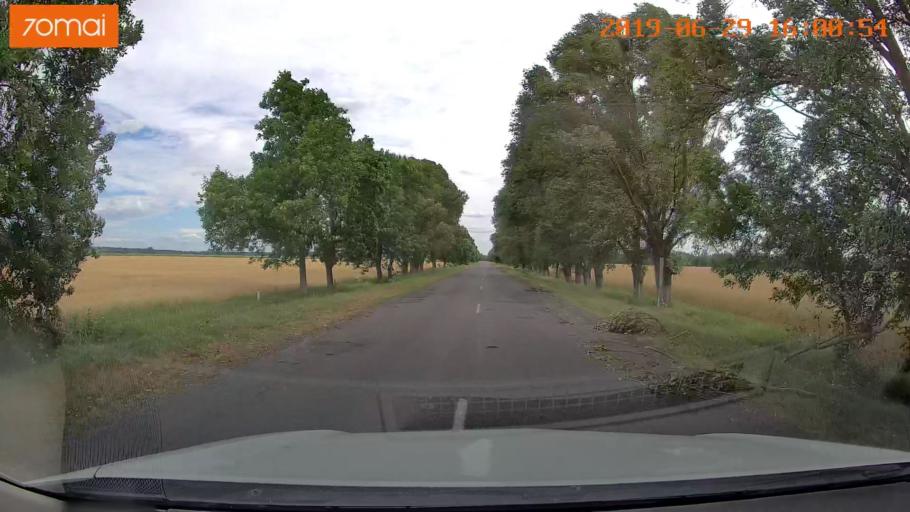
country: BY
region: Brest
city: Luninyets
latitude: 52.2544
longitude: 27.0170
